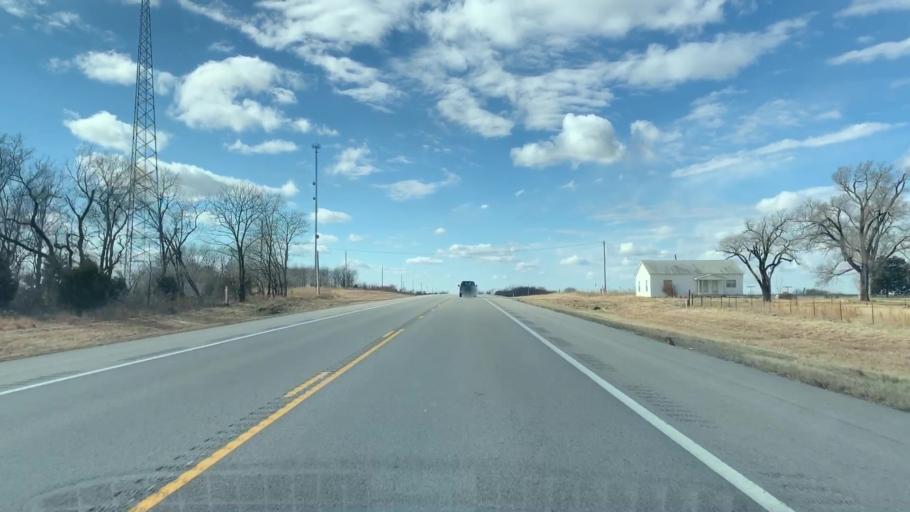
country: US
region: Kansas
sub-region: Labette County
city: Oswego
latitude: 37.3401
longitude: -95.0252
